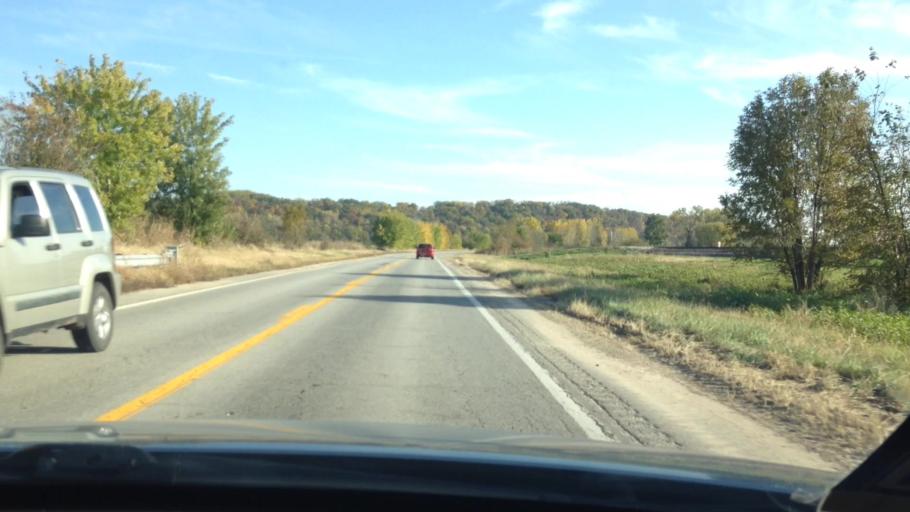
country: US
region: Kansas
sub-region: Leavenworth County
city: Lansing
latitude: 39.2608
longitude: -94.8121
